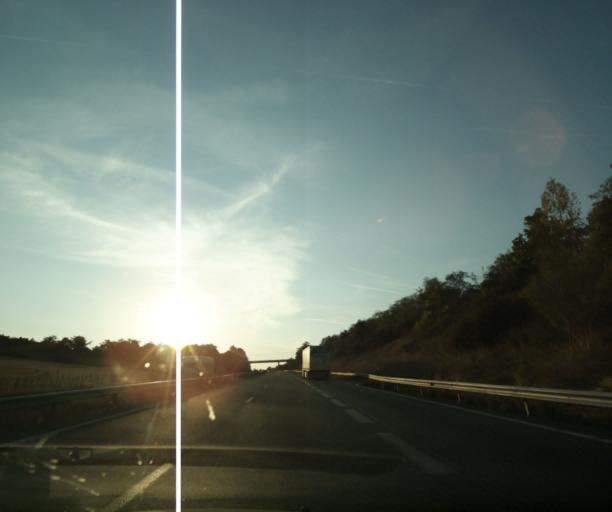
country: FR
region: Midi-Pyrenees
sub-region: Departement du Tarn-et-Garonne
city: Auvillar
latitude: 44.0686
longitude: 0.8452
